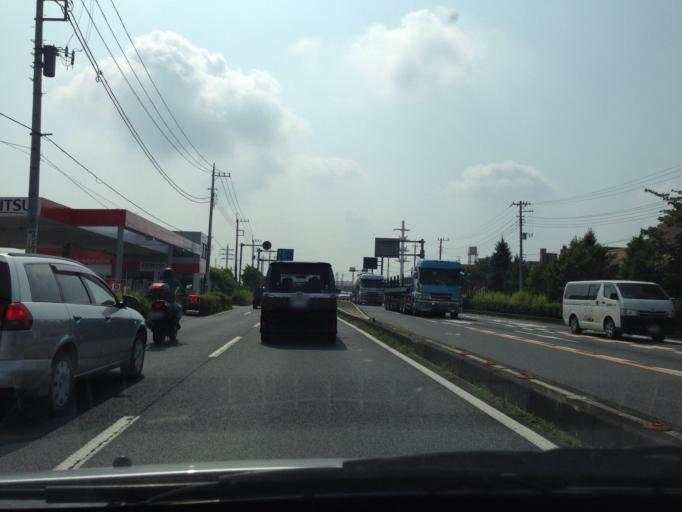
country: JP
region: Ibaraki
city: Ami
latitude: 36.0381
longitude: 140.2155
